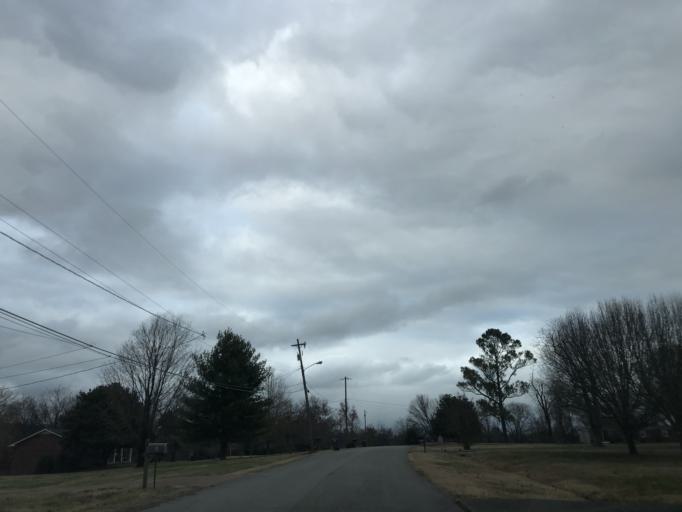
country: US
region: Tennessee
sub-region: Davidson County
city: Goodlettsville
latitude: 36.2979
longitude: -86.6835
